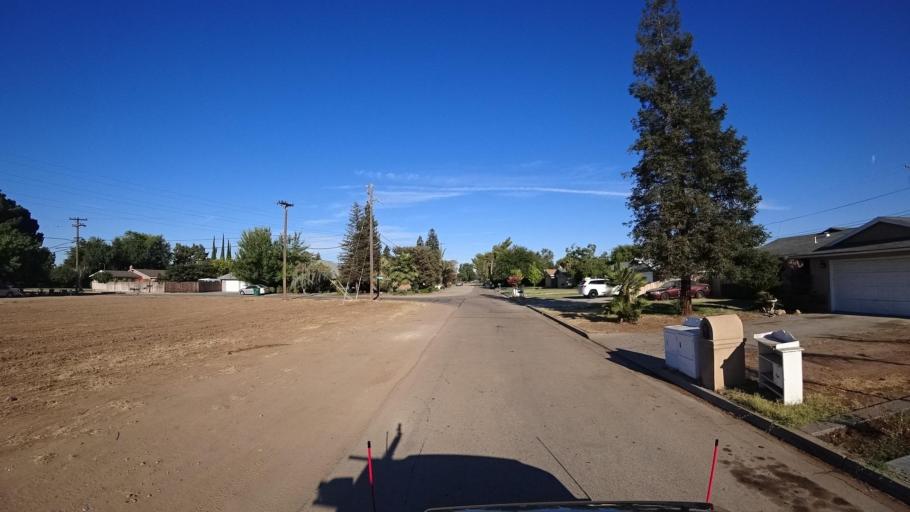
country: US
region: California
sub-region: Fresno County
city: Sunnyside
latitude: 36.7522
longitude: -119.7110
